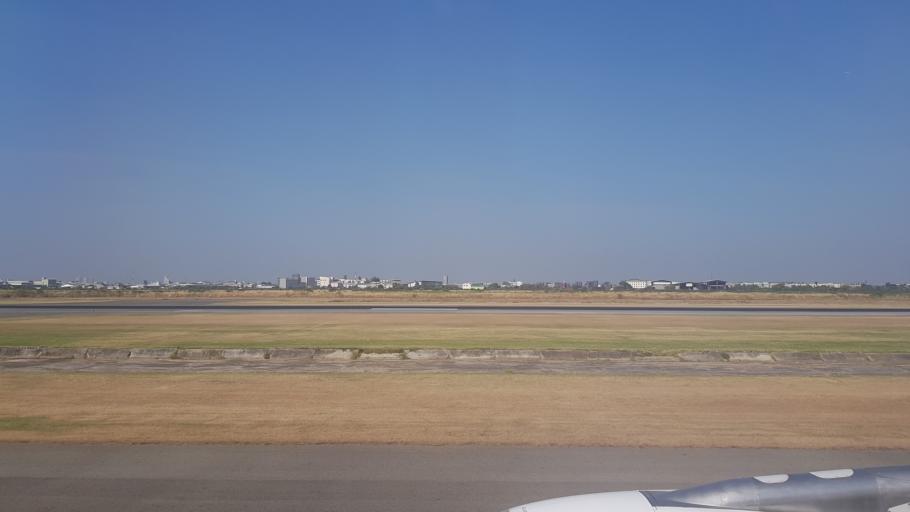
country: TH
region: Bangkok
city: Lat Krabang
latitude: 13.6763
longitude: 100.7379
